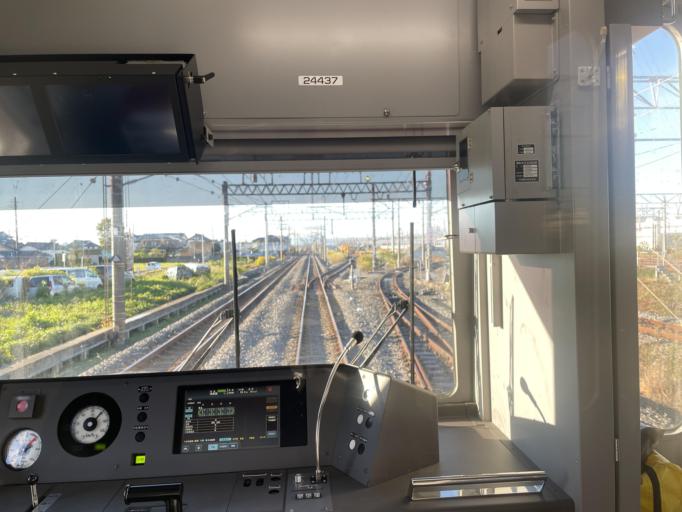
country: JP
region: Saitama
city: Kurihashi
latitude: 36.1192
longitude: 139.7058
